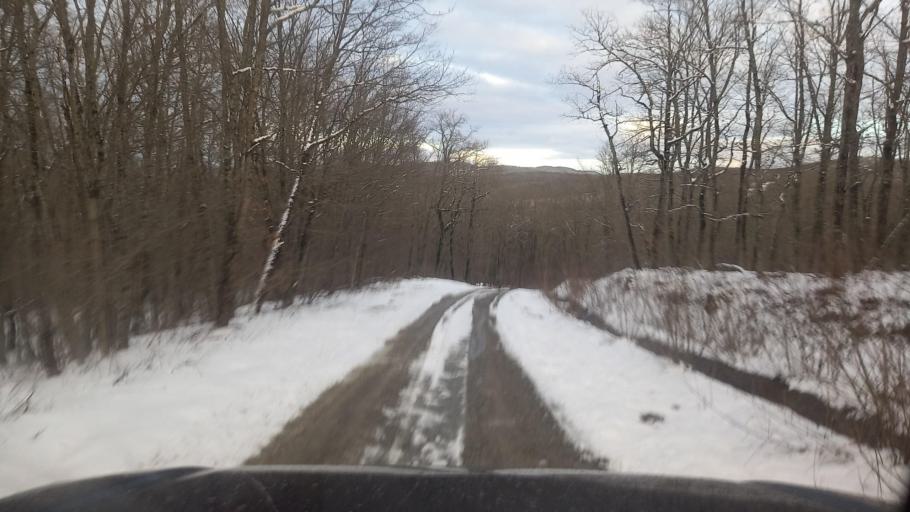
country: RU
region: Krasnodarskiy
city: Smolenskaya
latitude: 44.6798
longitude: 38.7771
